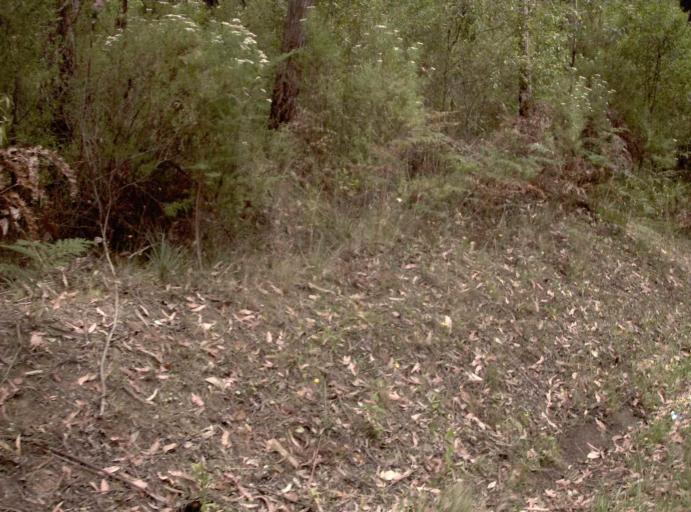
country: AU
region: Victoria
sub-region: Latrobe
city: Traralgon
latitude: -38.0339
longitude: 146.4195
